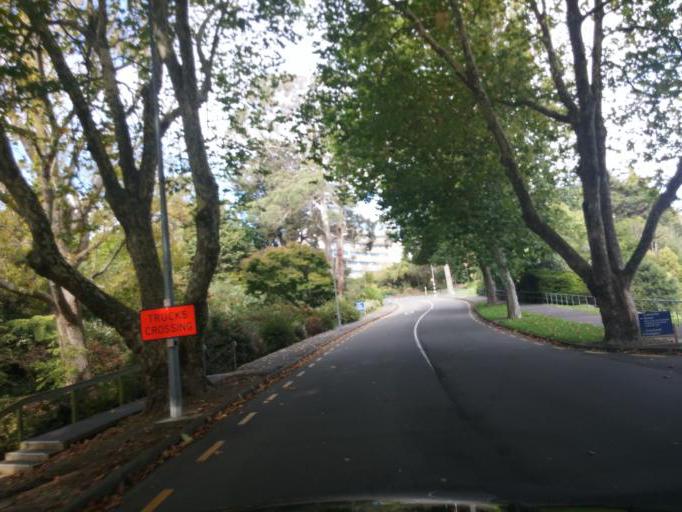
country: NZ
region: Manawatu-Wanganui
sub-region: Palmerston North City
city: Palmerston North
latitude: -40.3830
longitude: 175.6167
